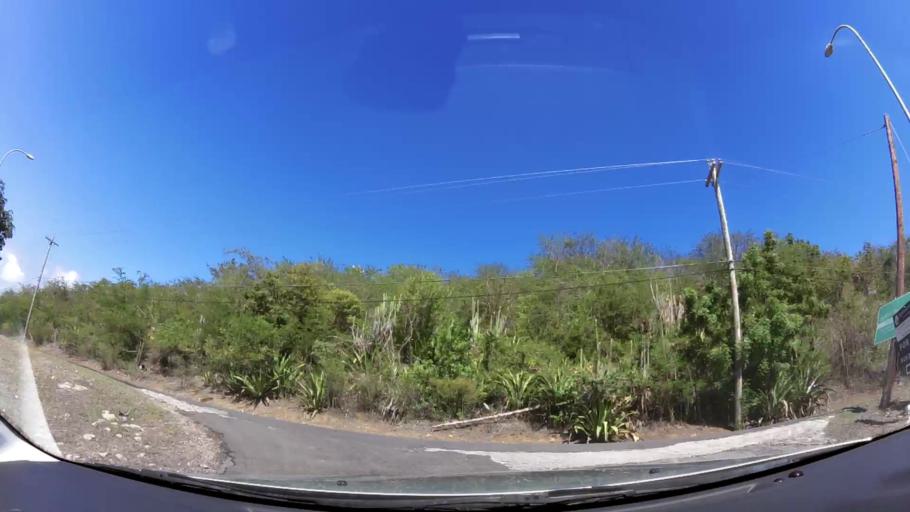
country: AG
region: Saint Paul
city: Falmouth
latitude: 17.0101
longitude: -61.7583
